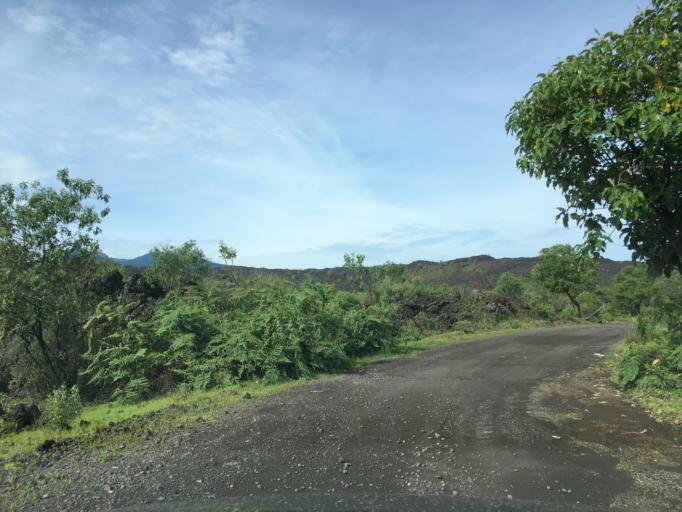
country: MX
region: Michoacan
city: Angahuan
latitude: 19.5272
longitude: -102.2464
